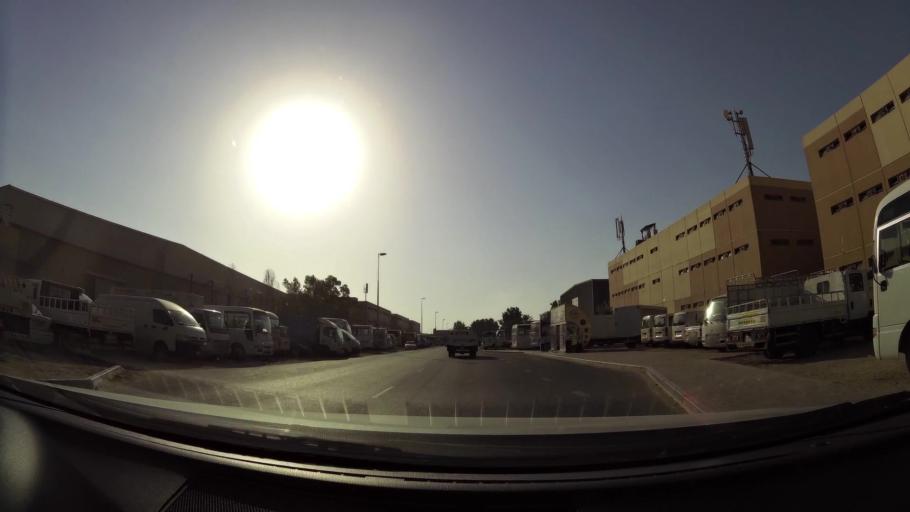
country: AE
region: Dubai
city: Dubai
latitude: 25.1325
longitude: 55.2503
